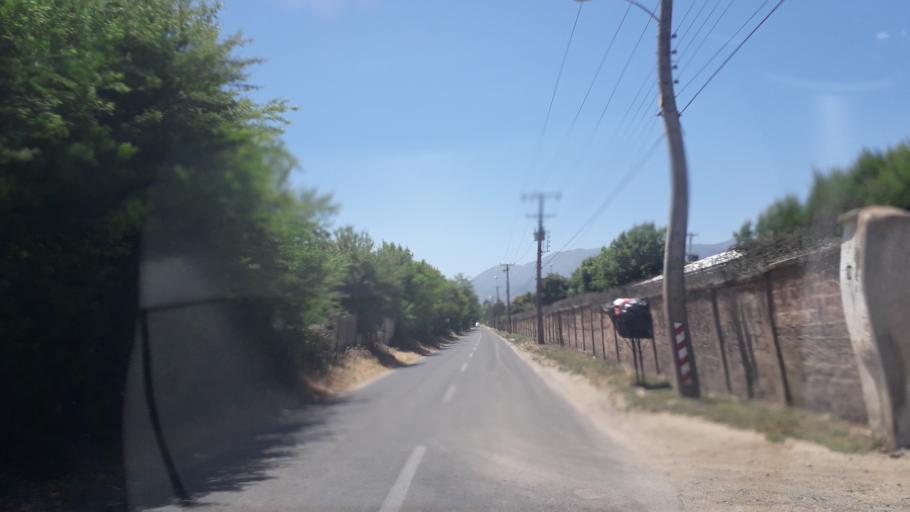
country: CL
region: Valparaiso
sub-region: Provincia de Quillota
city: Quillota
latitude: -32.9217
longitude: -71.2422
